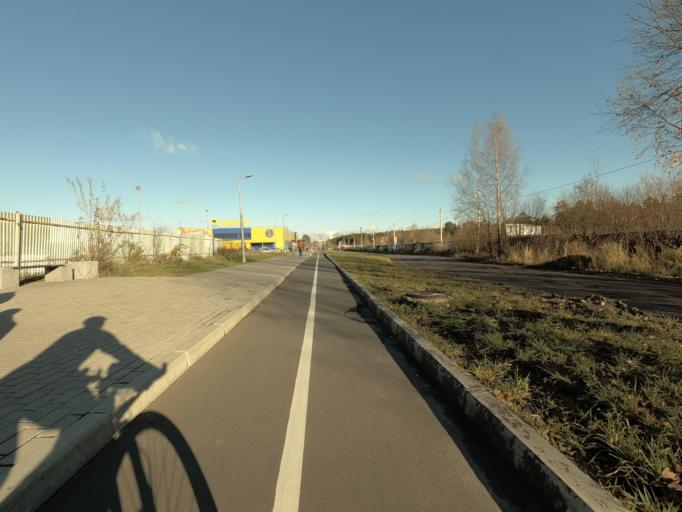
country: RU
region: Leningrad
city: Vsevolozhsk
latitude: 60.0203
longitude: 30.6031
